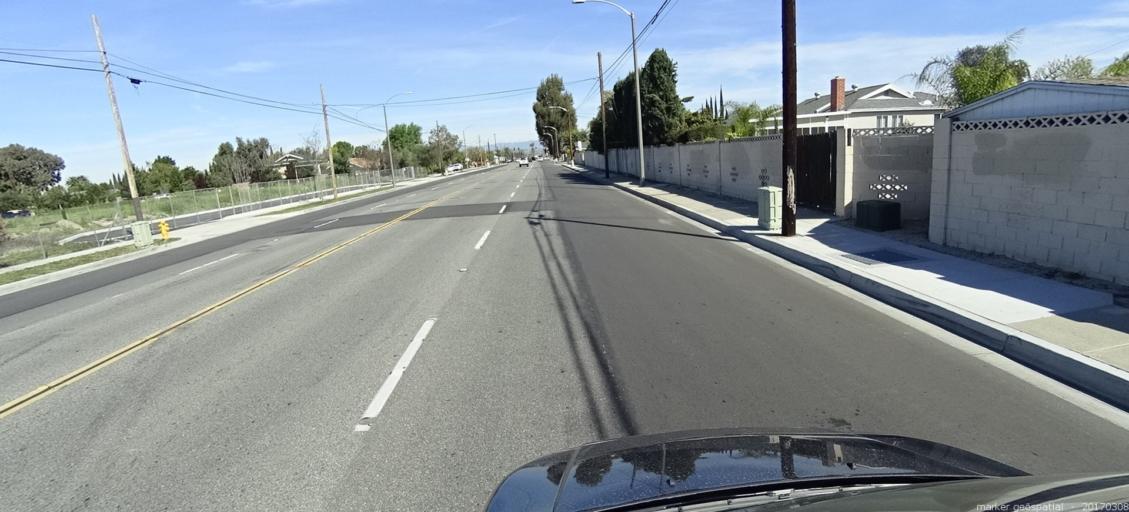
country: US
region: California
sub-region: Orange County
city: Buena Park
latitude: 33.8367
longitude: -117.9848
